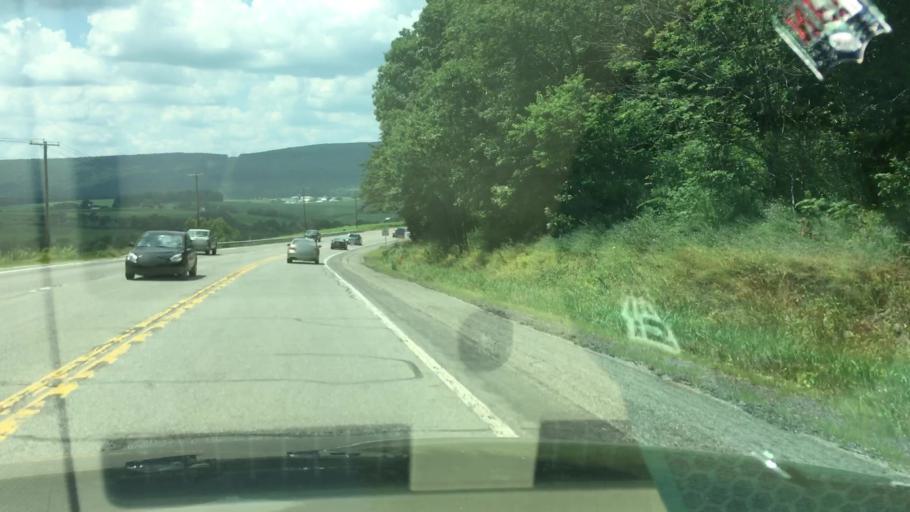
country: US
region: Pennsylvania
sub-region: Schuylkill County
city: Ashland
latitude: 40.7233
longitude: -76.3842
